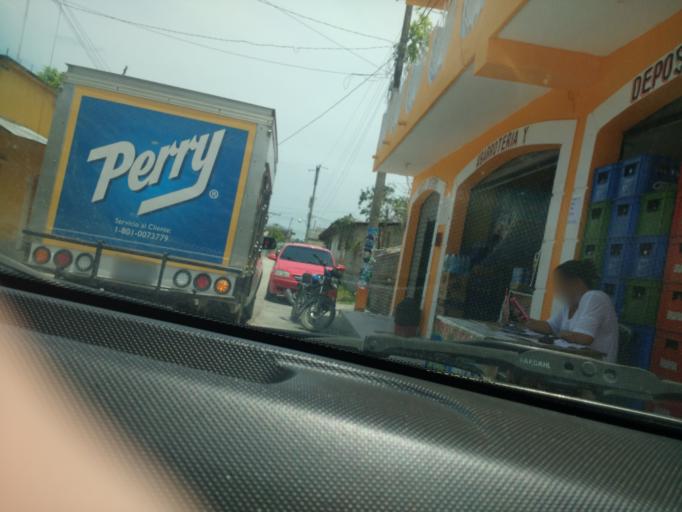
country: GT
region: Peten
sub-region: Municipio de Flores
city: Flores
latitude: 16.9248
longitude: -89.9011
